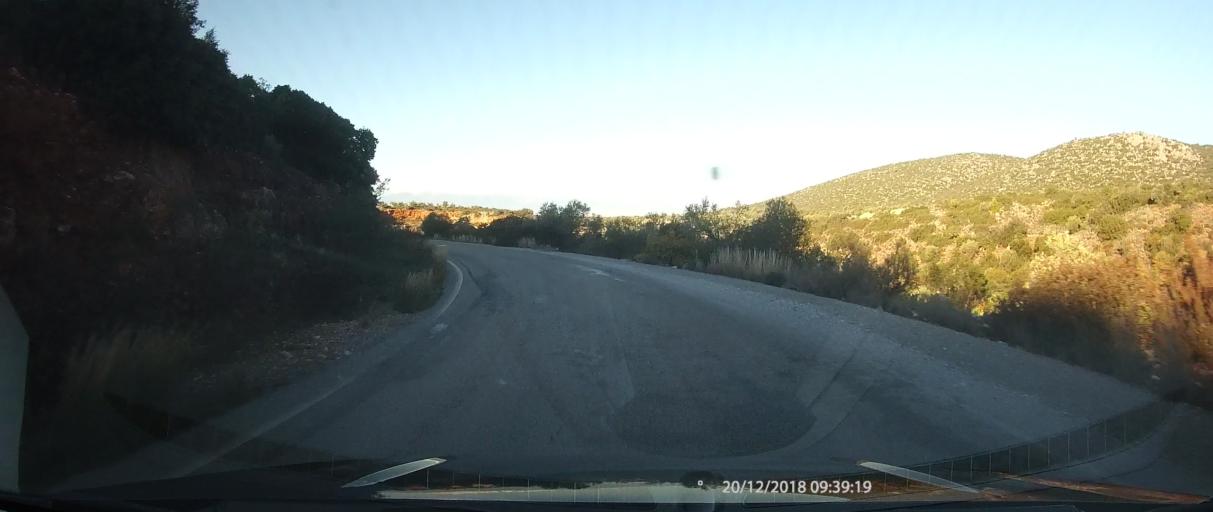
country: GR
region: Peloponnese
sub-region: Nomos Lakonias
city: Yerakion
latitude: 36.9393
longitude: 22.7777
